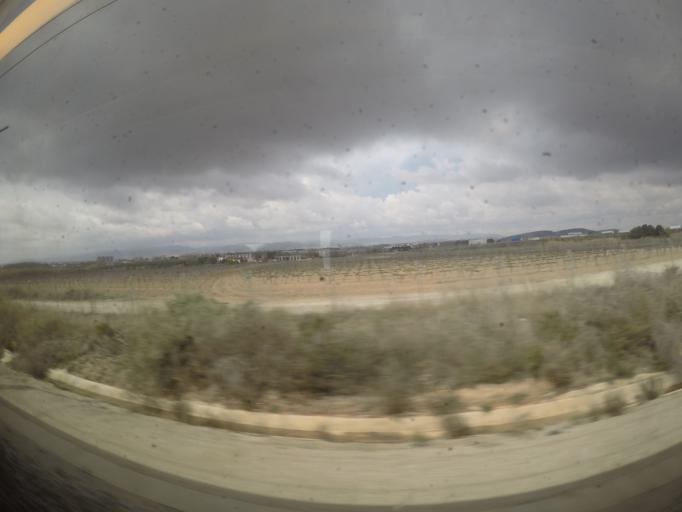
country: ES
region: Catalonia
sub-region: Provincia de Barcelona
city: Castellet
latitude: 41.3050
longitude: 1.6433
